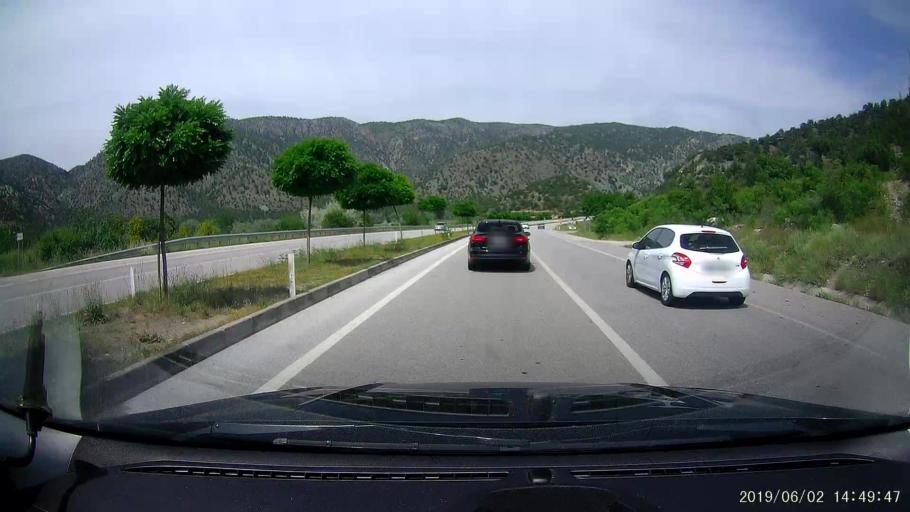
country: TR
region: Corum
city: Hacihamza
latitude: 41.0692
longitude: 34.5065
